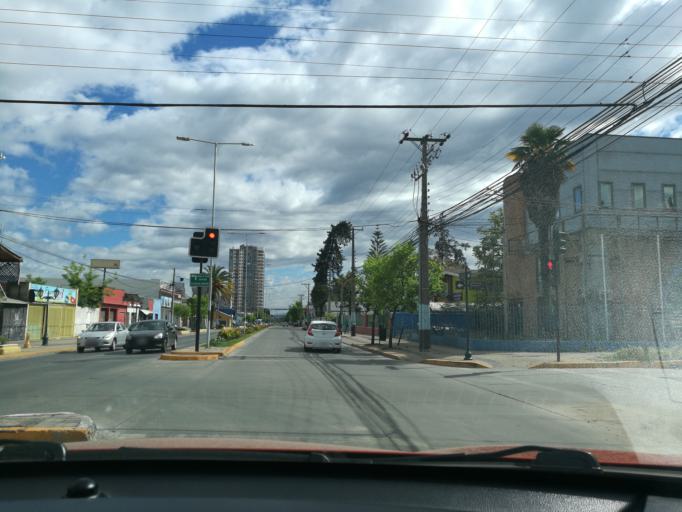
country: CL
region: O'Higgins
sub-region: Provincia de Cachapoal
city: Rancagua
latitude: -34.1746
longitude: -70.7362
